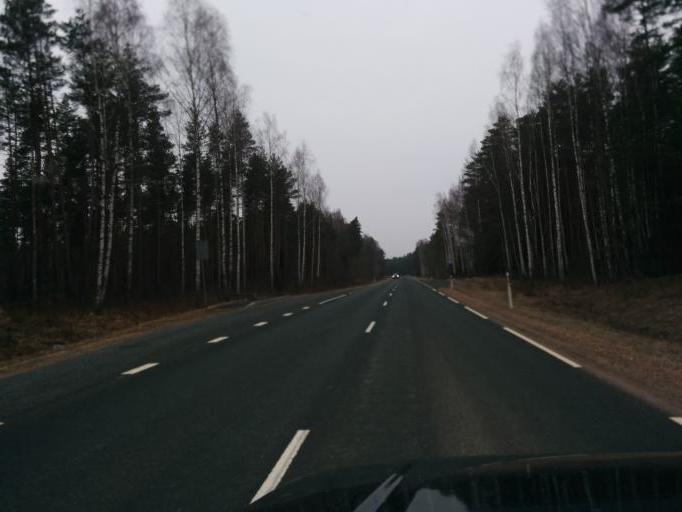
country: LV
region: Ogre
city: Ogre
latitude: 56.7942
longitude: 24.5991
